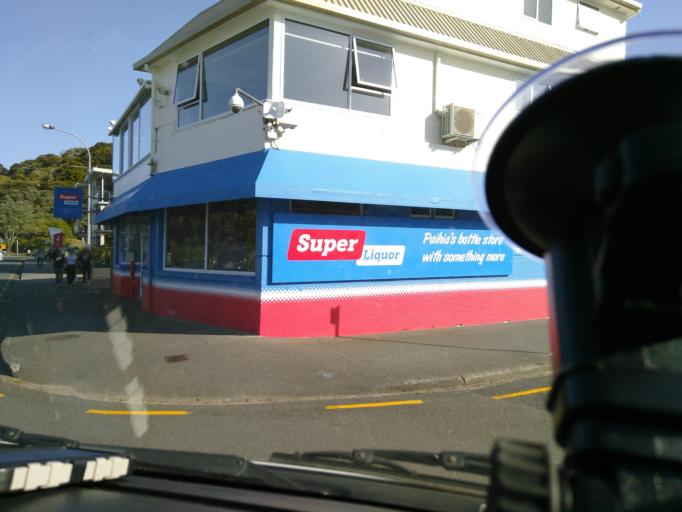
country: NZ
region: Northland
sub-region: Far North District
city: Paihia
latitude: -35.2846
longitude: 174.0957
